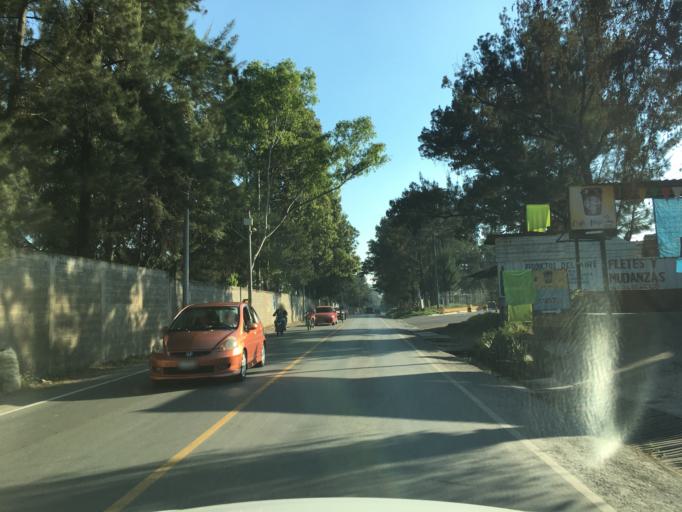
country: GT
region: Guatemala
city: Villa Nueva
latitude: 14.5314
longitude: -90.6166
